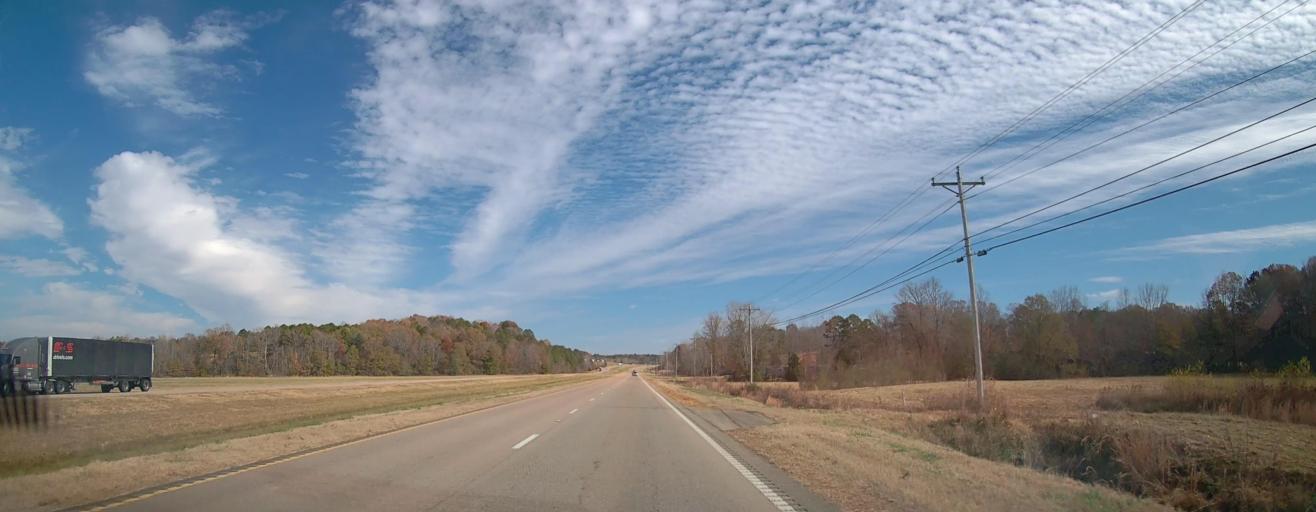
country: US
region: Mississippi
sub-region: Tippah County
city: Ripley
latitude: 34.9543
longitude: -88.8655
